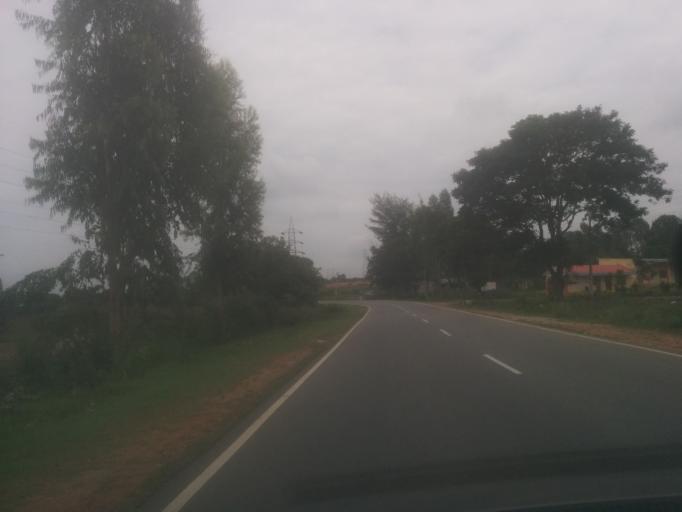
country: IN
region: Karnataka
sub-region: Hassan
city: Belur
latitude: 13.1632
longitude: 75.8943
